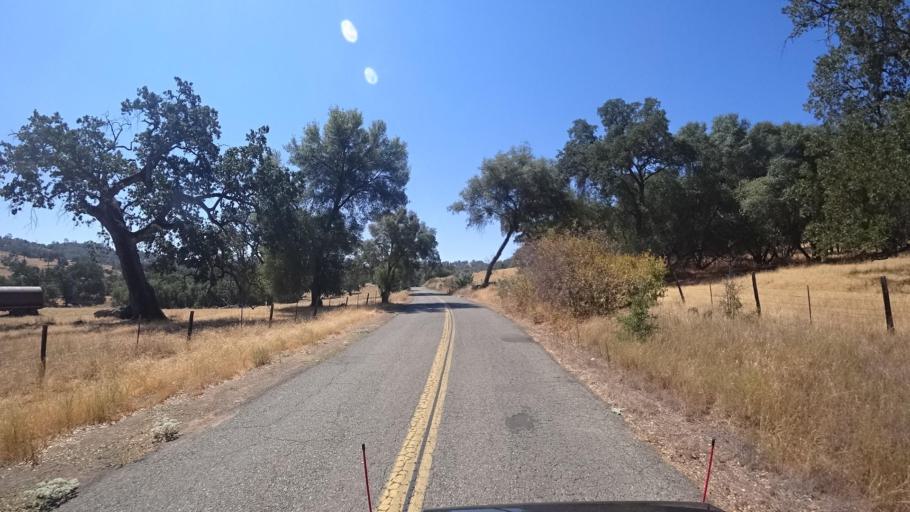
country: US
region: California
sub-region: Mariposa County
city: Mariposa
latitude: 37.3887
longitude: -119.9697
